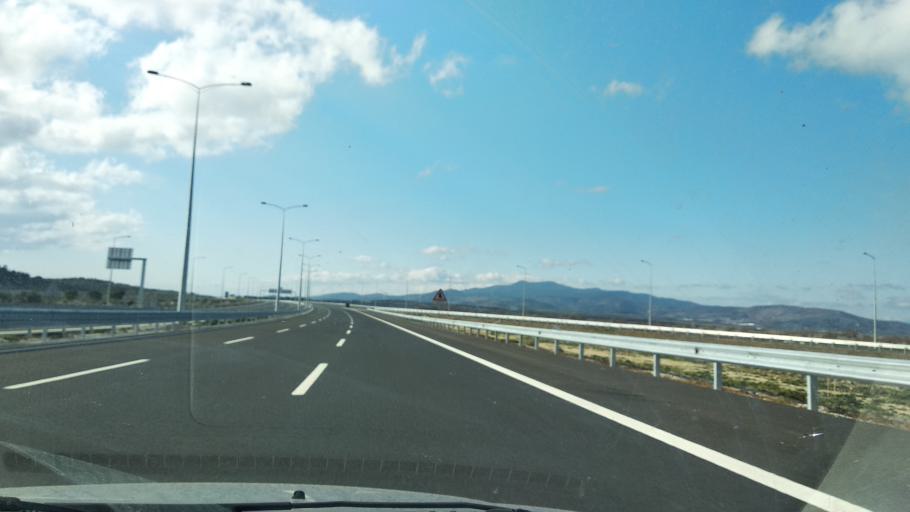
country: TR
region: Izmir
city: Zeytindag
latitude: 38.9725
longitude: 27.0414
